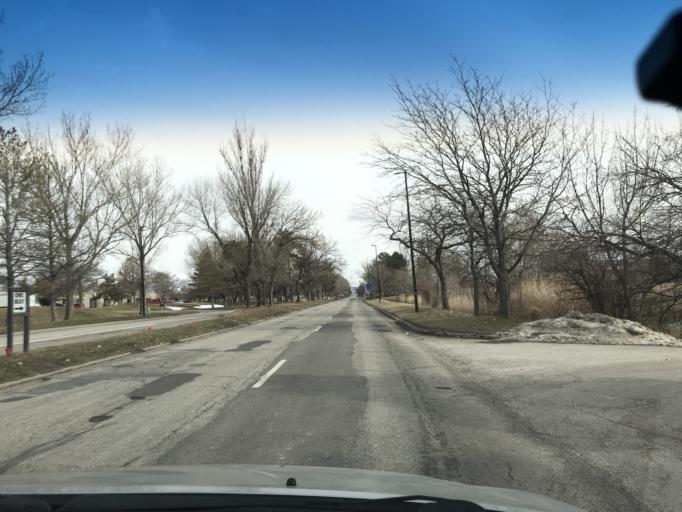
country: US
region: Utah
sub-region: Salt Lake County
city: West Valley City
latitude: 40.7763
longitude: -112.0143
